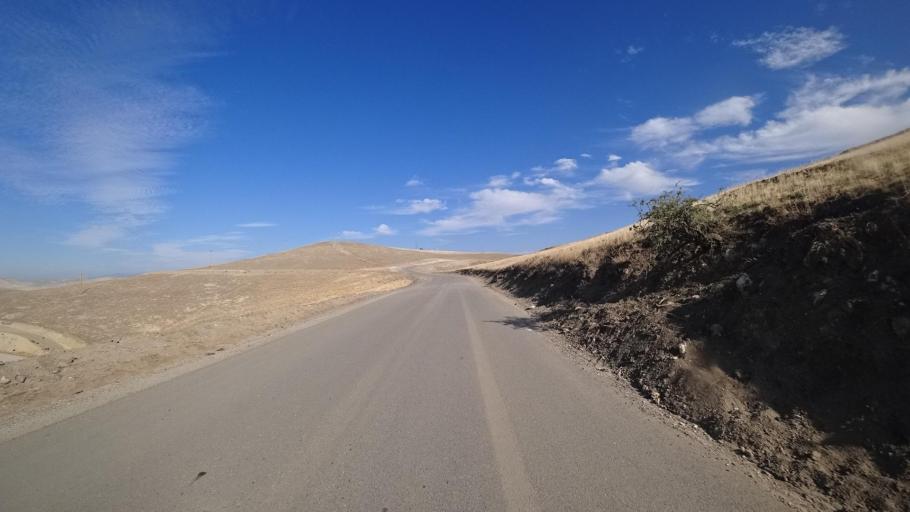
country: US
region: California
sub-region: Kern County
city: Oildale
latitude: 35.4860
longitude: -118.8810
